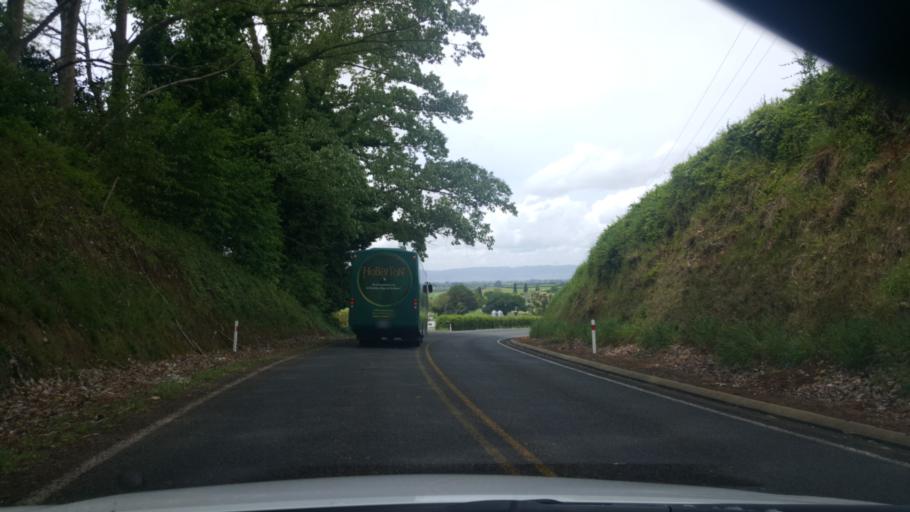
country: NZ
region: Waikato
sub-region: Matamata-Piako District
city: Matamata
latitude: -37.8768
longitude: 175.7005
